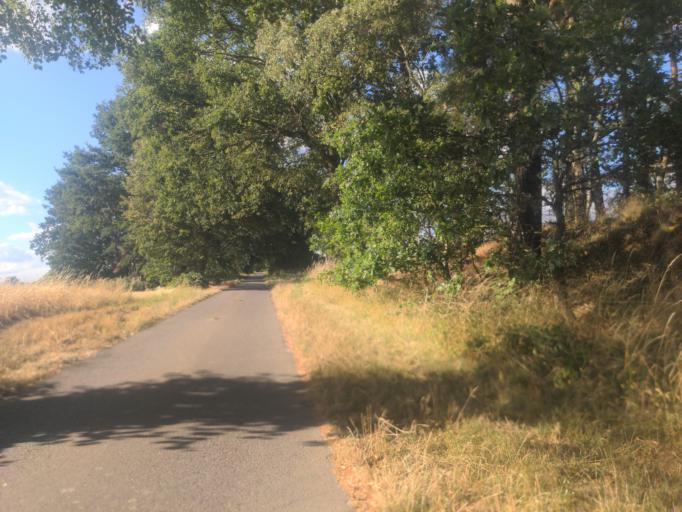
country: DE
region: Lower Saxony
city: Tosterglope
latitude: 53.2021
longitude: 10.8241
